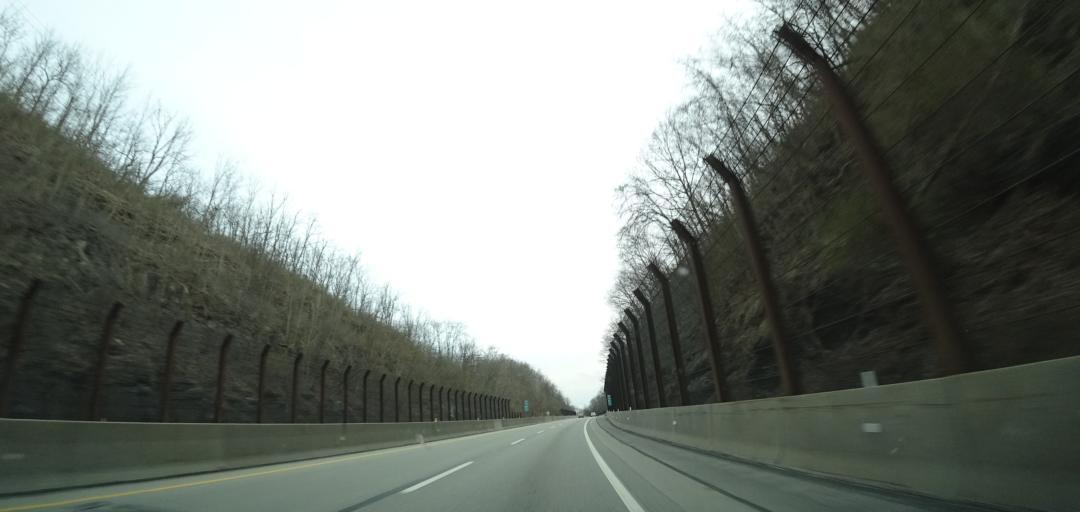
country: US
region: Pennsylvania
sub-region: Allegheny County
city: Springdale
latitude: 40.5093
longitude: -79.7897
